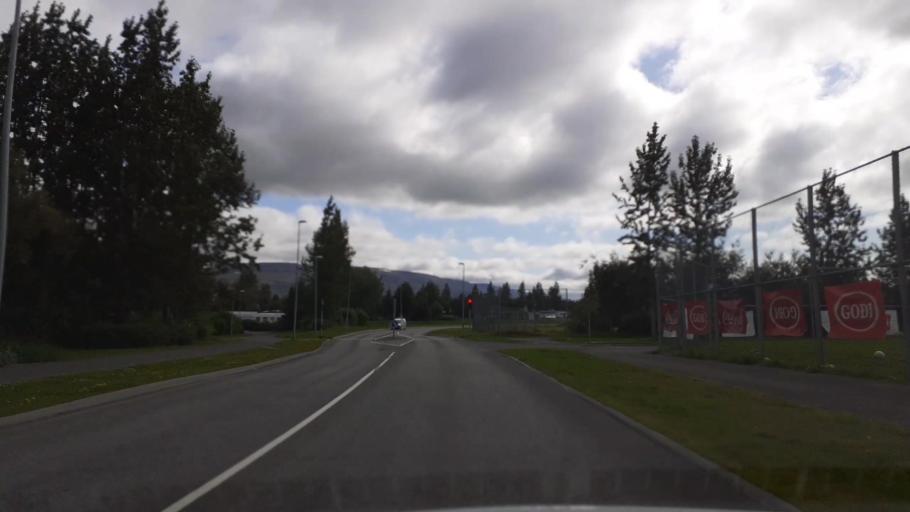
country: IS
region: Northeast
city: Akureyri
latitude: 65.6770
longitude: -18.1128
